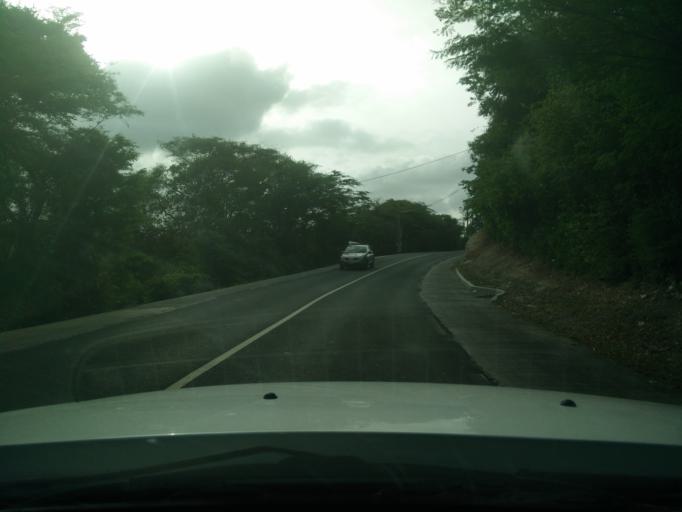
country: GP
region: Guadeloupe
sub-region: Guadeloupe
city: Saint-Francois
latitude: 16.2536
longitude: -61.3251
